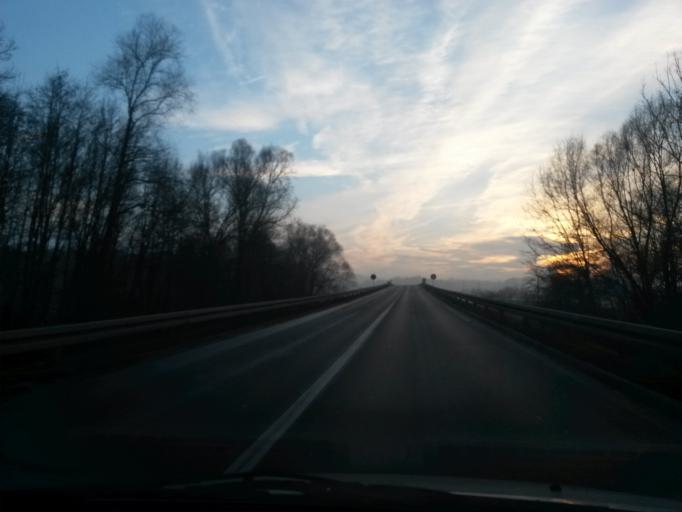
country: HR
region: Varazdinska
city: Ludbreg
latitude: 46.2495
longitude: 16.6339
